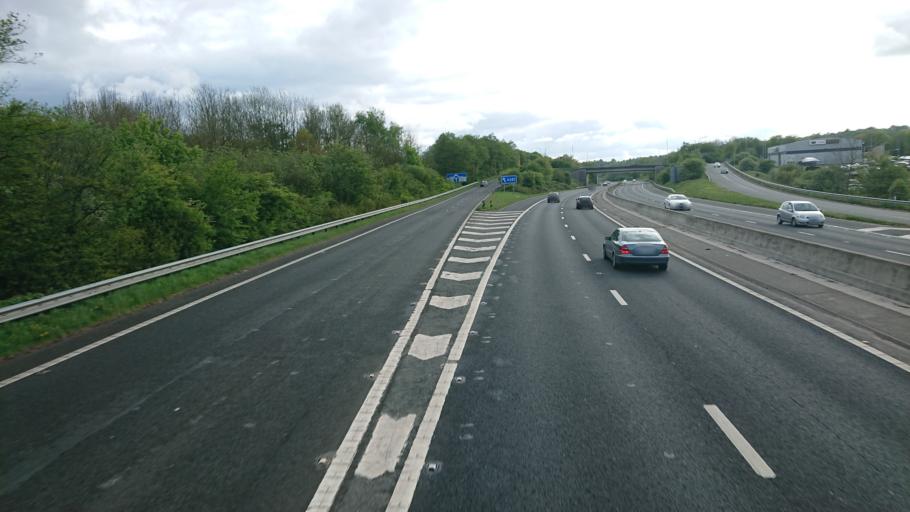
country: GB
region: England
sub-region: Lancashire
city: Brierfield
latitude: 53.8321
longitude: -2.2299
